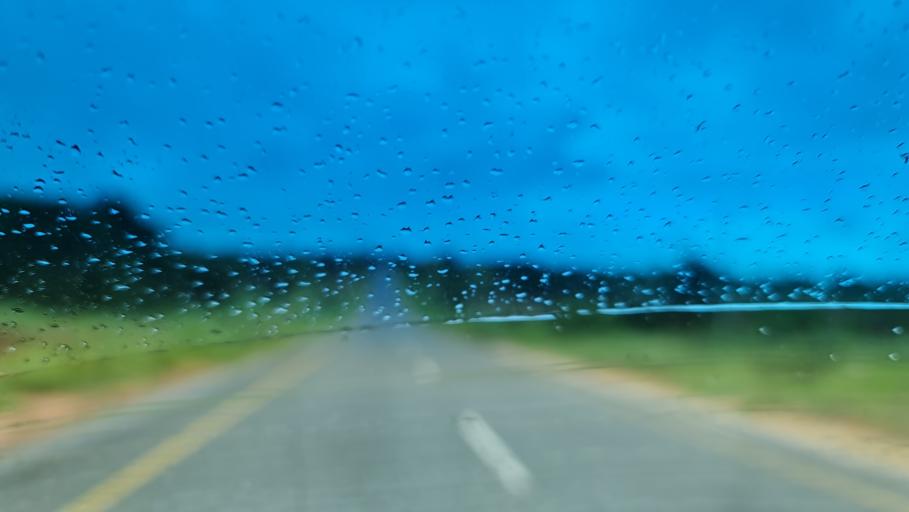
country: MZ
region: Nampula
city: Nampula
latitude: -15.4937
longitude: 39.3328
